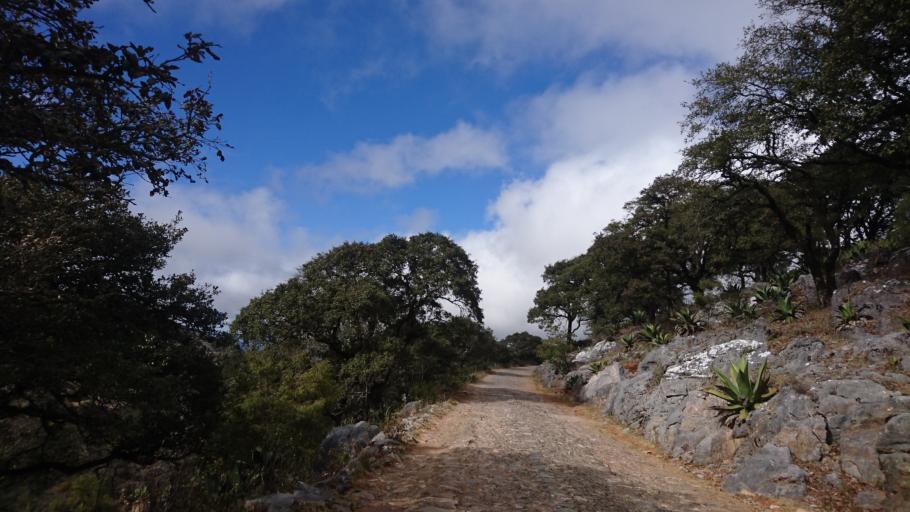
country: MX
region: San Luis Potosi
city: Zaragoza
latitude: 22.0723
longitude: -100.6418
